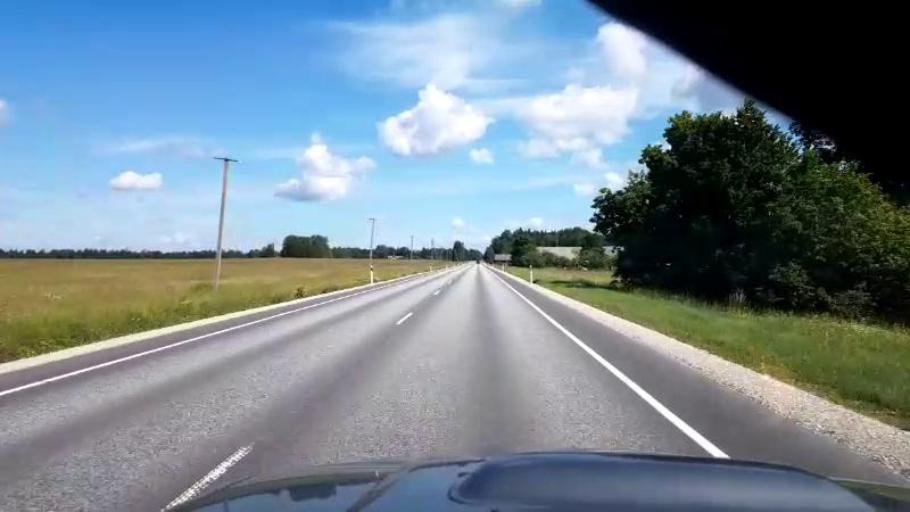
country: EE
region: Jaervamaa
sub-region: Paide linn
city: Paide
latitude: 58.9730
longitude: 25.6649
